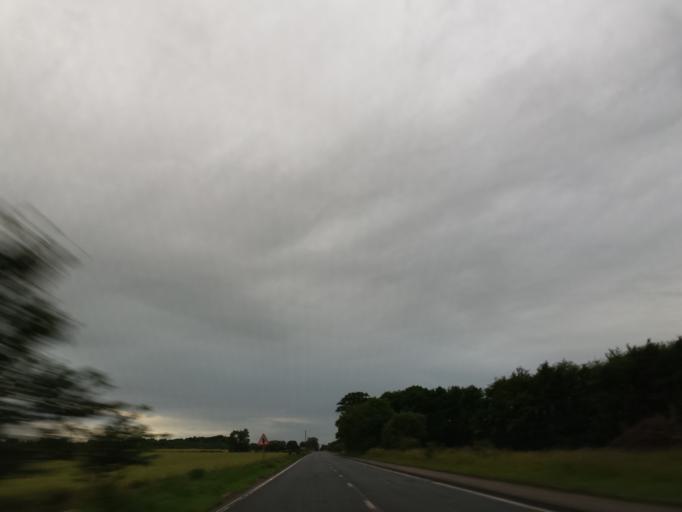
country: GB
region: Scotland
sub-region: East Lothian
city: Dunbar
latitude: 55.9902
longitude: -2.5845
